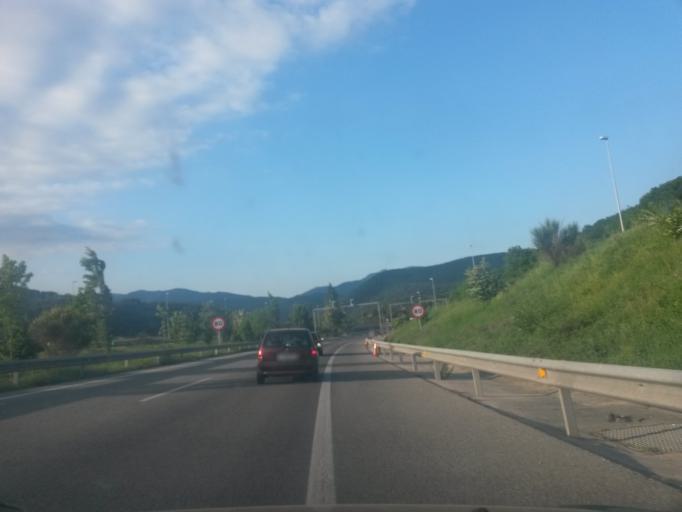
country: ES
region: Catalonia
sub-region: Provincia de Girona
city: Sant Joan les Fonts
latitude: 42.2118
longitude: 2.5399
